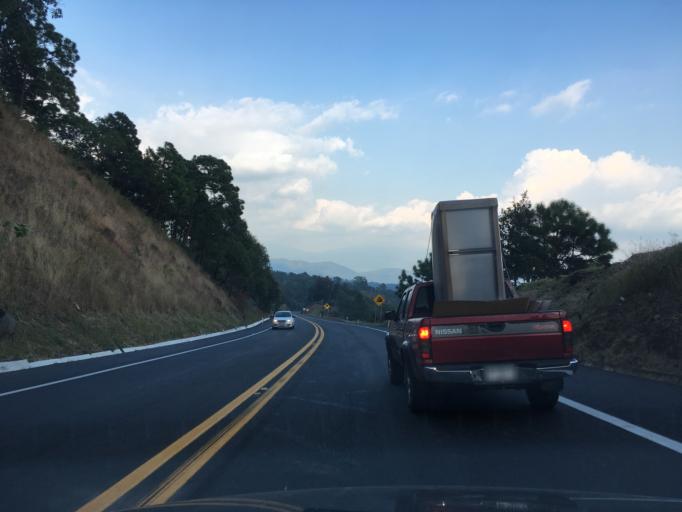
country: MX
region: Michoacan
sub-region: Uruapan
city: Toreo Bajo (El Toreo Bajo)
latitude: 19.4150
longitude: -101.9742
